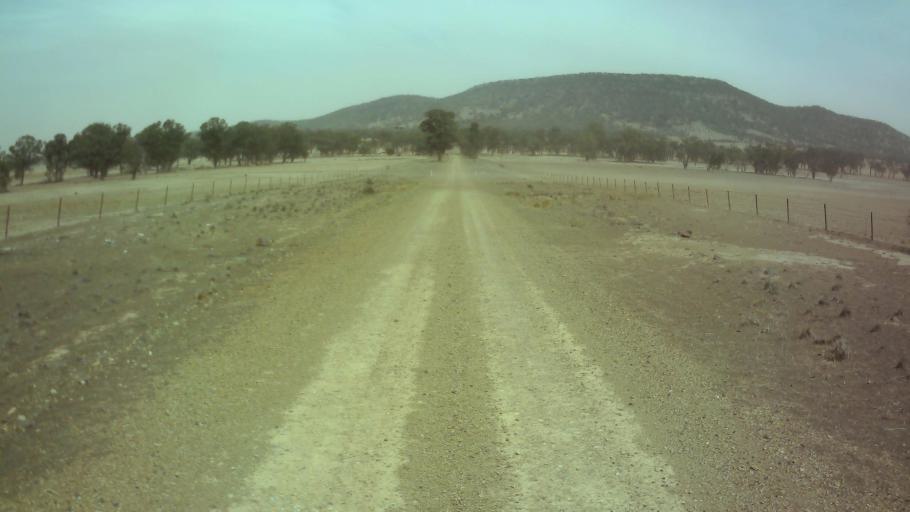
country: AU
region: New South Wales
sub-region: Weddin
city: Grenfell
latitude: -33.7444
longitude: 147.9680
